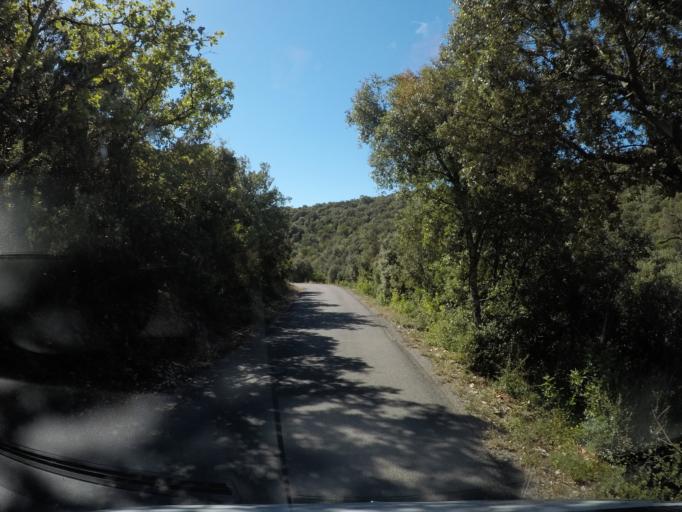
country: FR
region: Languedoc-Roussillon
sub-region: Departement de l'Herault
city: Vailhauques
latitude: 43.7170
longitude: 3.6798
